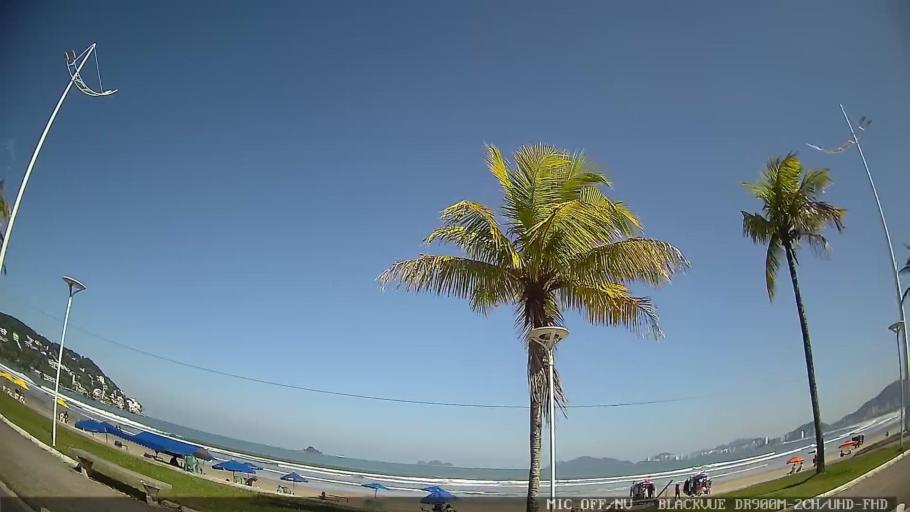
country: BR
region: Sao Paulo
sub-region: Guaruja
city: Guaruja
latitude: -23.9870
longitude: -46.2065
